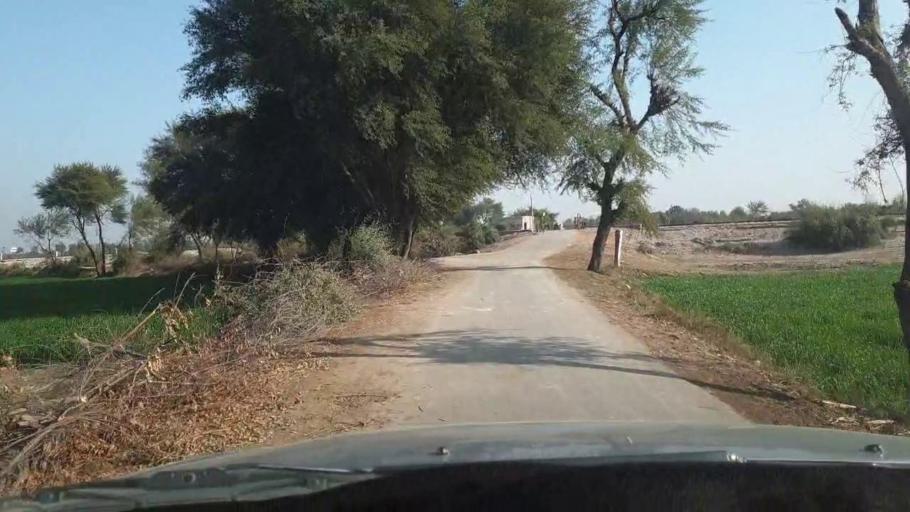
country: PK
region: Sindh
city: Mirpur Mathelo
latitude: 28.0198
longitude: 69.5844
